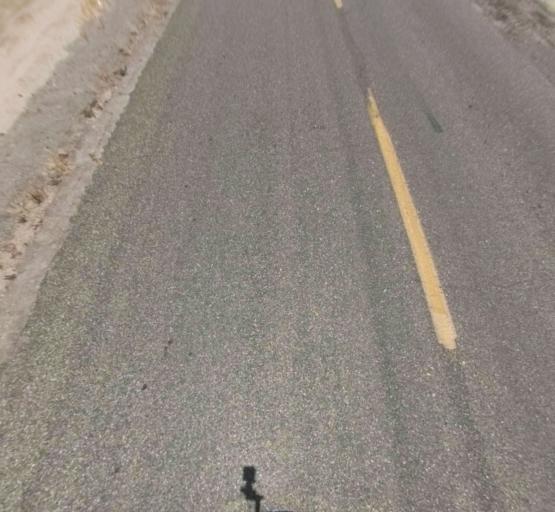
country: US
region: California
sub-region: Madera County
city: Parkwood
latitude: 36.8691
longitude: -120.0922
